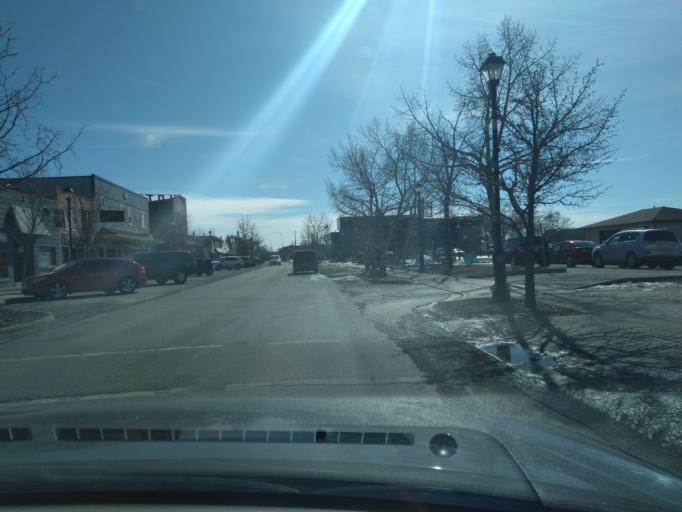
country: CA
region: Alberta
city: Cochrane
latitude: 51.1906
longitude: -114.4710
